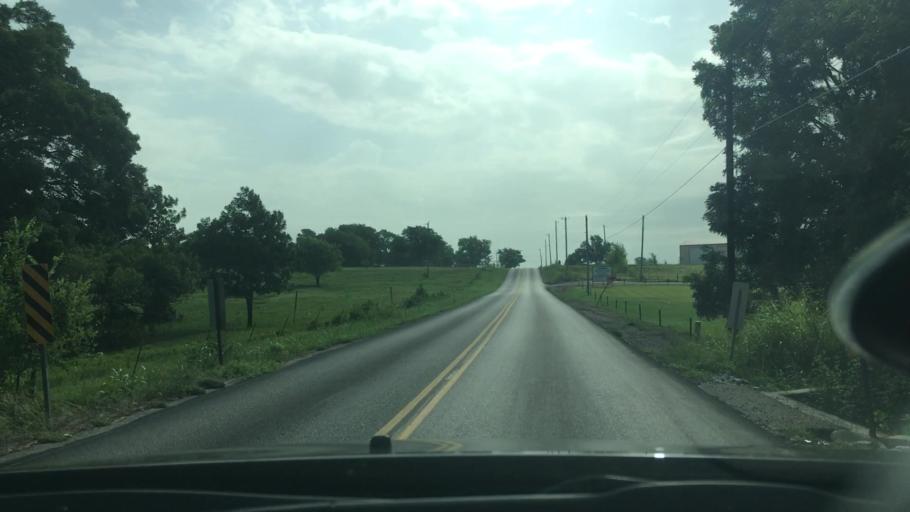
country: US
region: Oklahoma
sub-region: Carter County
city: Lone Grove
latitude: 34.2020
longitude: -97.2072
